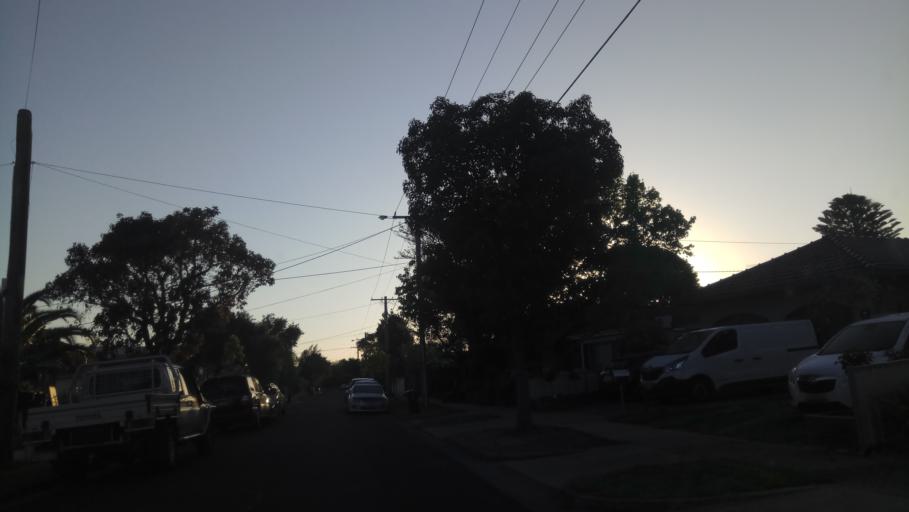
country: AU
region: Victoria
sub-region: Hobsons Bay
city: Altona
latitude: -37.8720
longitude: 144.8144
